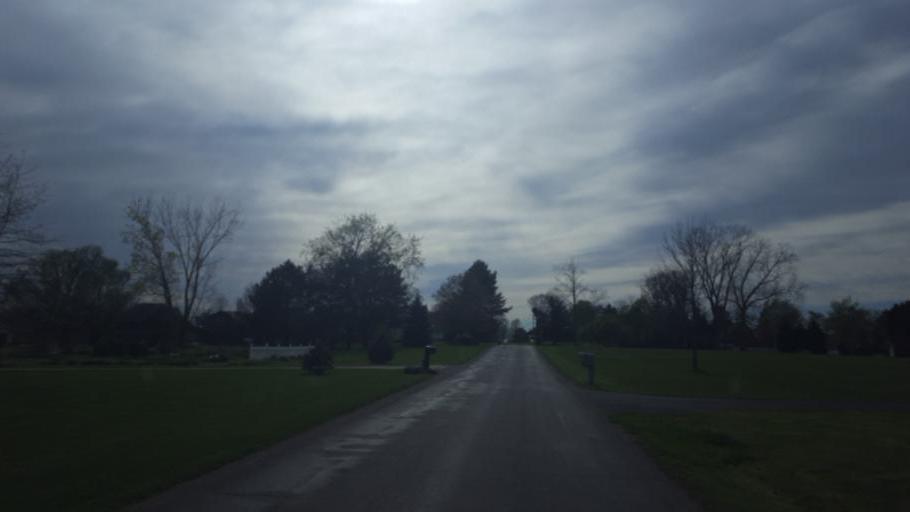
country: US
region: Ohio
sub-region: Crawford County
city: Crestline
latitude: 40.7478
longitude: -82.7198
